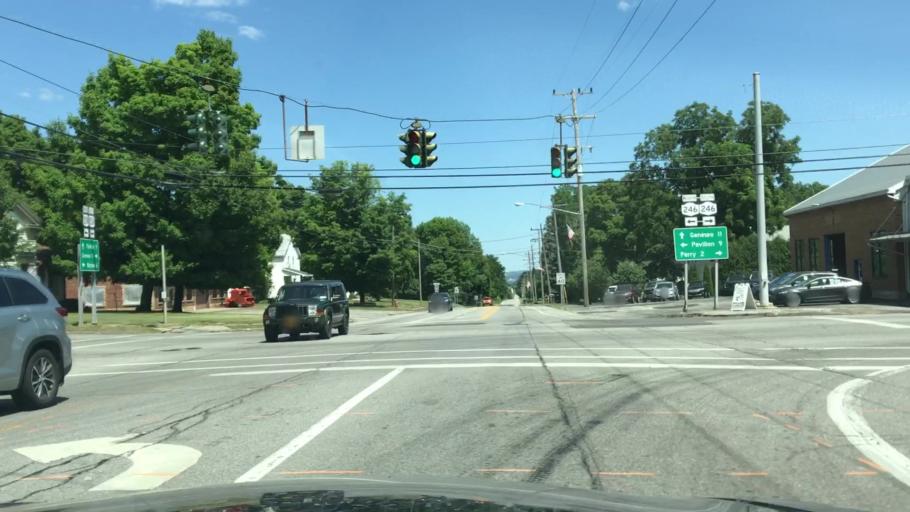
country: US
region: New York
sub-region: Wyoming County
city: Perry
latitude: 42.7487
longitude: -78.0060
